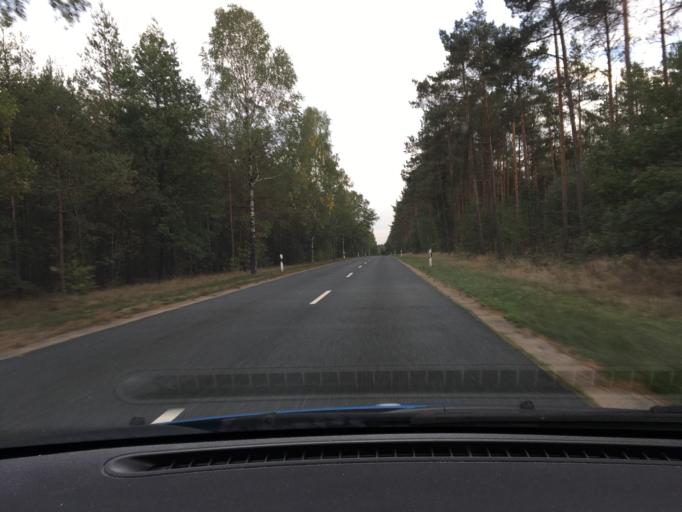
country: DE
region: Lower Saxony
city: Bispingen
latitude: 53.0810
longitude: 10.0577
